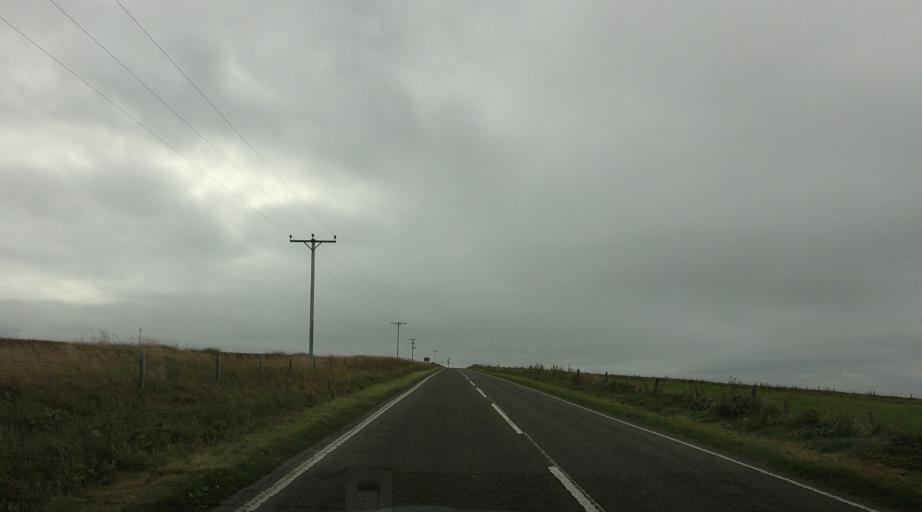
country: GB
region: Scotland
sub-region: Orkney Islands
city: Orkney
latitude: 58.7769
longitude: -2.9602
